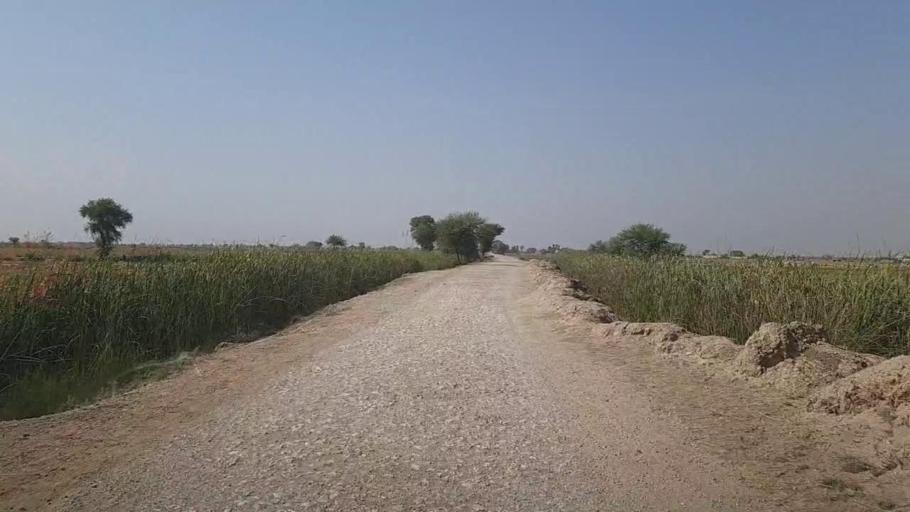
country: PK
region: Sindh
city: Kandhkot
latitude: 28.4010
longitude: 69.2631
